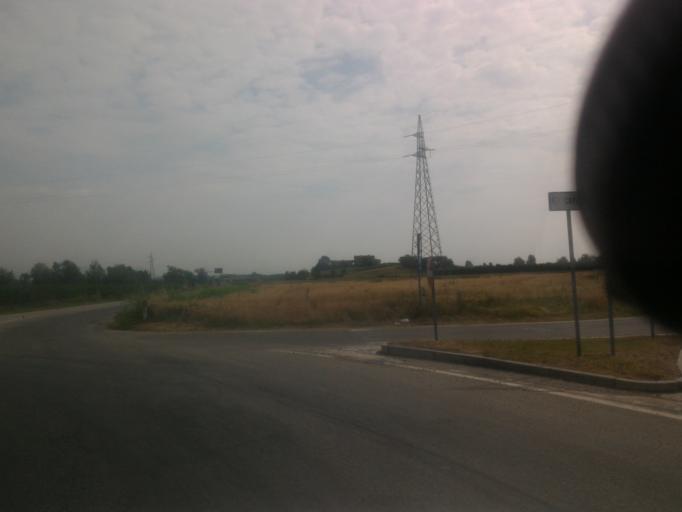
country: IT
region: Piedmont
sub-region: Provincia di Torino
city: Bricherasio
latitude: 44.8254
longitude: 7.3127
